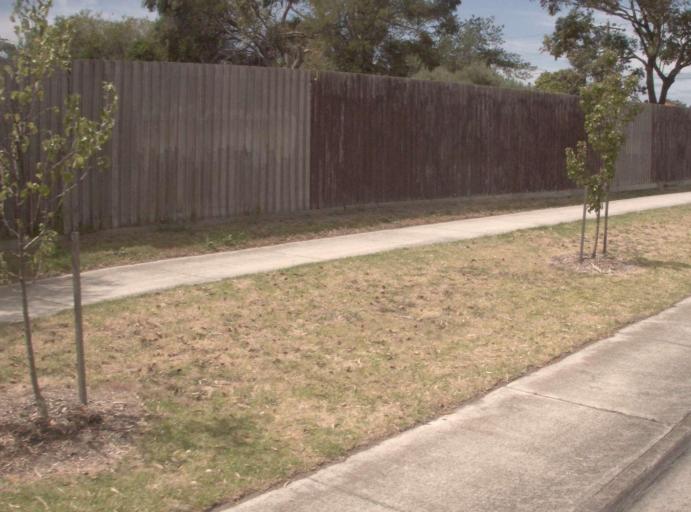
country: AU
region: Victoria
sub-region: Greater Dandenong
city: Keysborough
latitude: -37.9922
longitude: 145.1574
